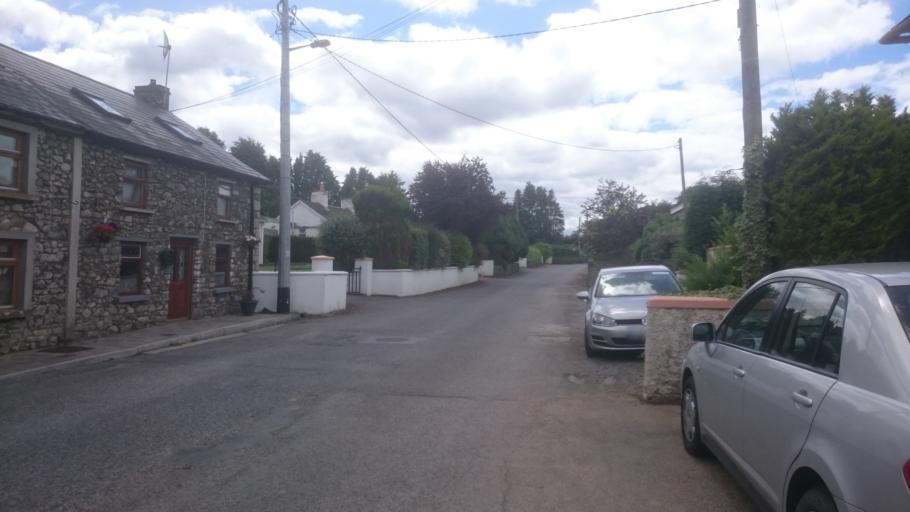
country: IE
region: Leinster
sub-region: Kilkenny
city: Kilkenny
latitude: 52.5393
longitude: -7.2733
